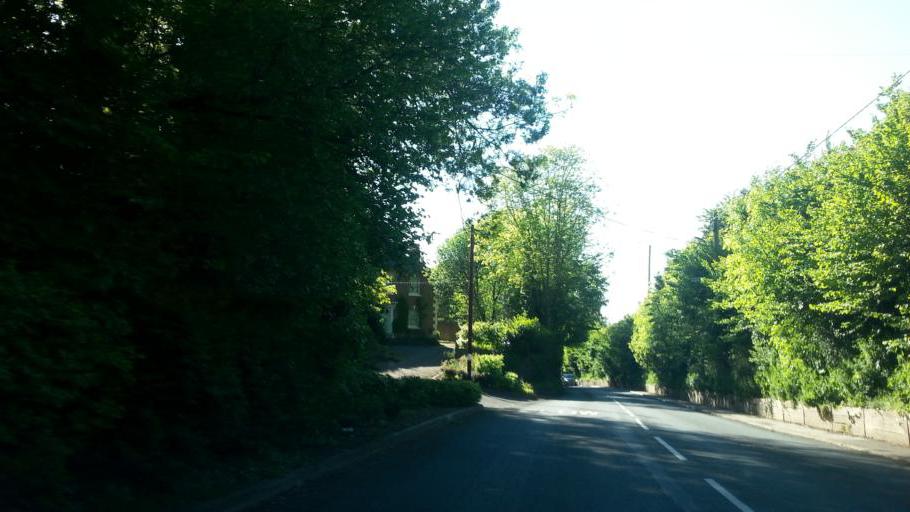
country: GB
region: England
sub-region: Somerset
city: Castle Cary
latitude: 51.0965
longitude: -2.5164
